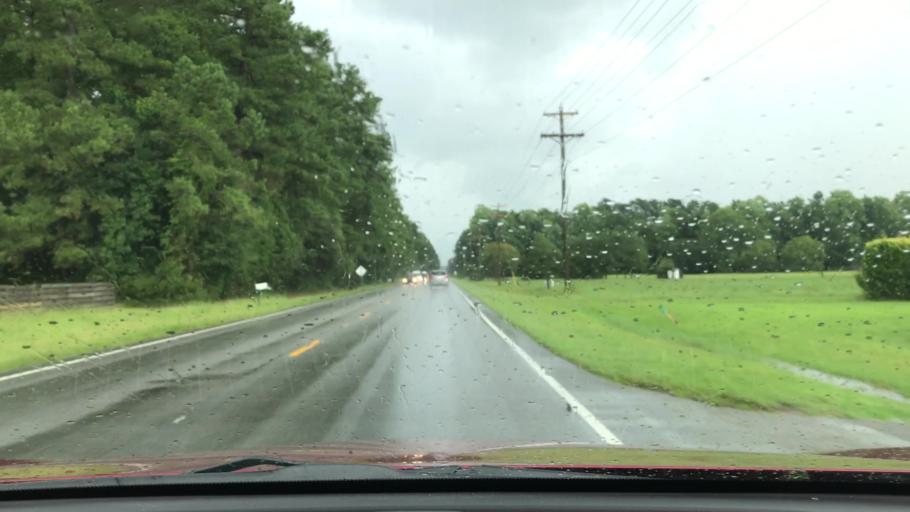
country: US
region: South Carolina
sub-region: Horry County
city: Socastee
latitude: 33.7022
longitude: -79.1070
